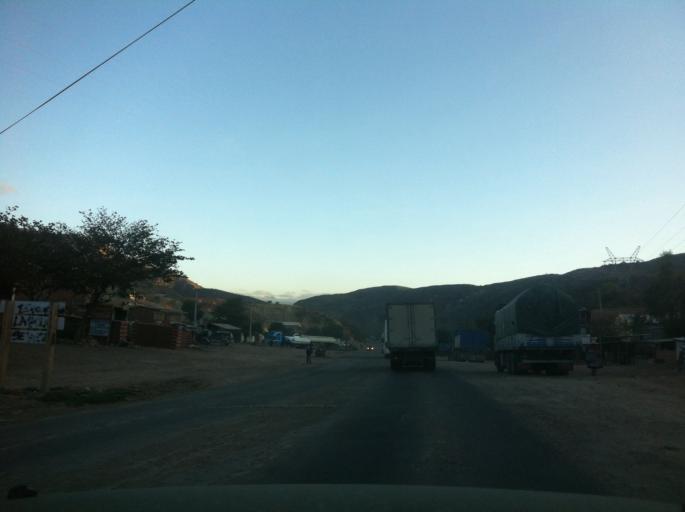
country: BO
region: Cochabamba
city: Sipe Sipe
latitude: -17.5629
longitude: -66.3441
